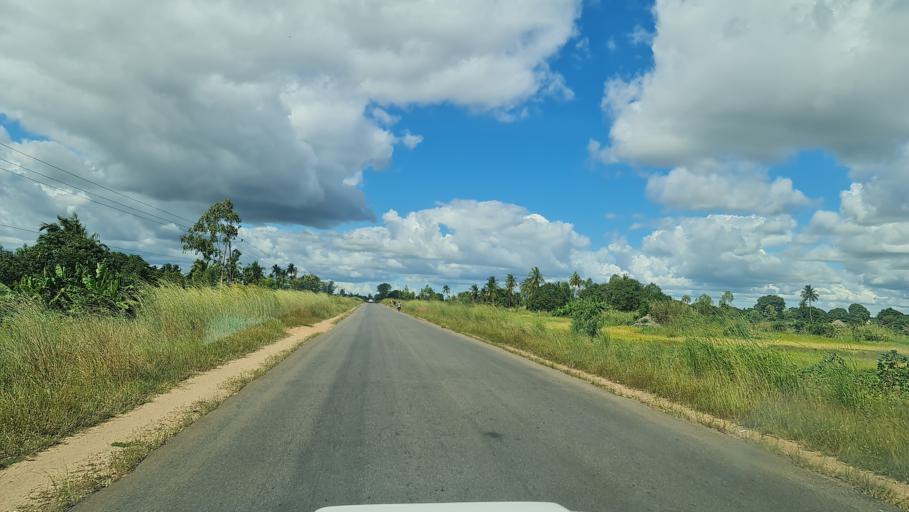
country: MZ
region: Zambezia
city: Quelimane
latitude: -17.5911
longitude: 36.7669
